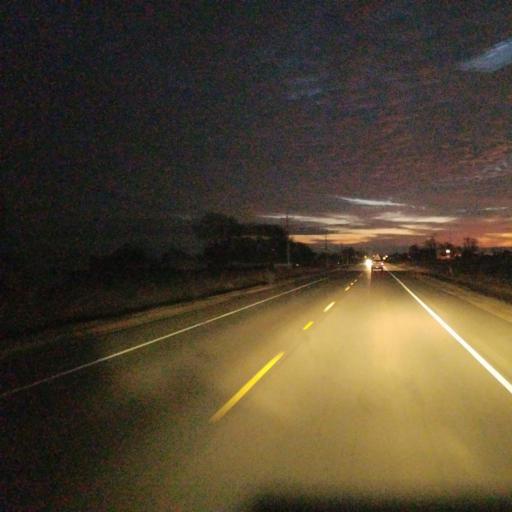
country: US
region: Illinois
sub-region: Peoria County
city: Hanna City
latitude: 40.6973
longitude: -89.8407
